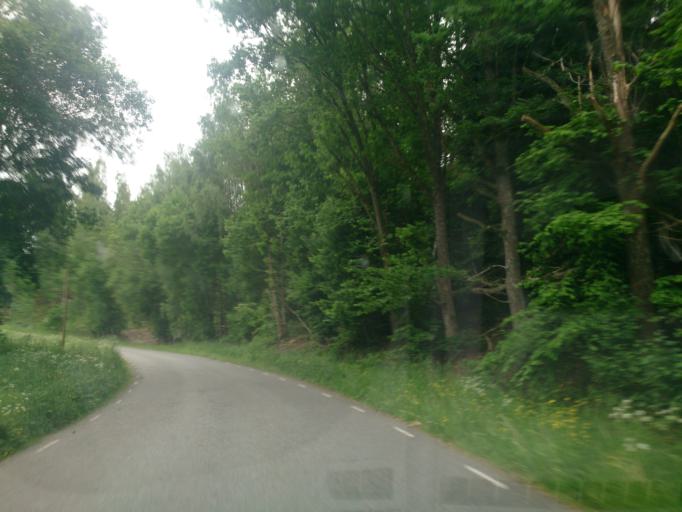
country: SE
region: OEstergoetland
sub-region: Atvidabergs Kommun
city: Atvidaberg
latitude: 58.2998
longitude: 16.0938
